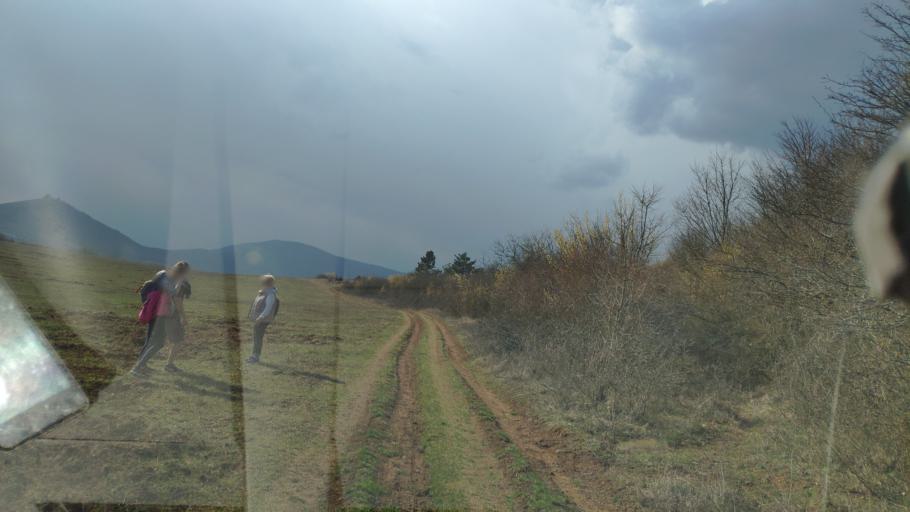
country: SK
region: Kosicky
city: Moldava nad Bodvou
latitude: 48.6170
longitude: 20.9138
